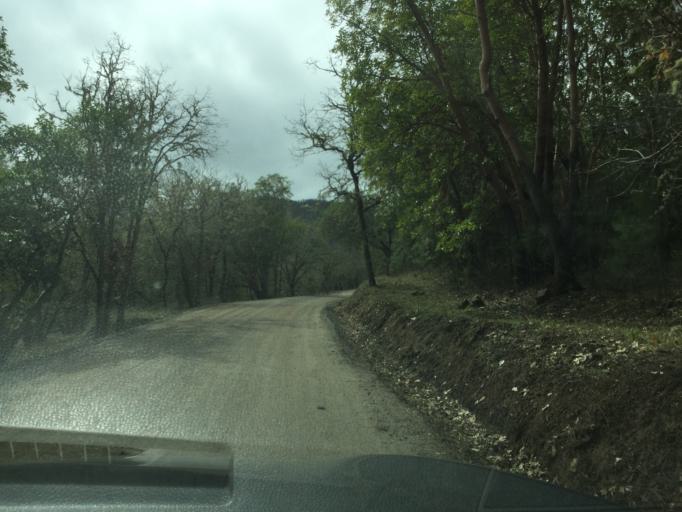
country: US
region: Oregon
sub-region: Jackson County
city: Gold Hill
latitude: 42.4526
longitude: -123.0074
